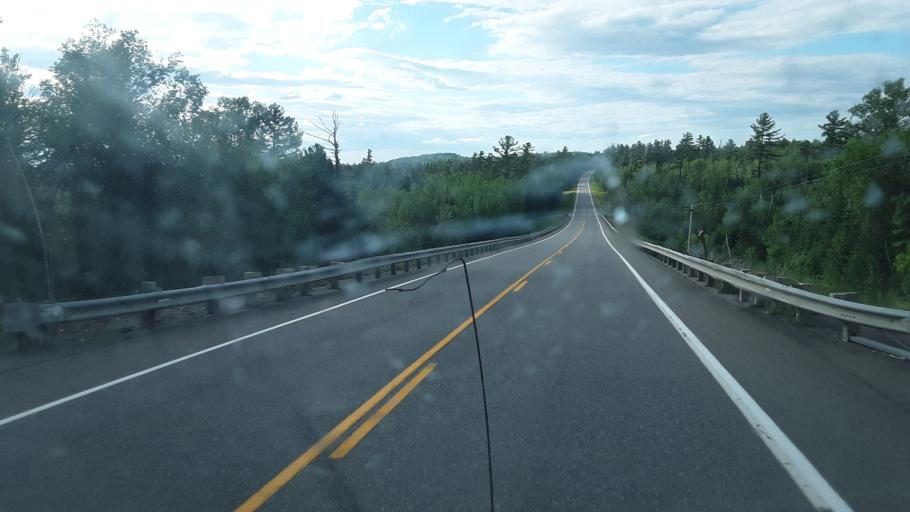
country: US
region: Maine
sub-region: Penobscot County
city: Patten
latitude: 46.4201
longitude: -68.3746
